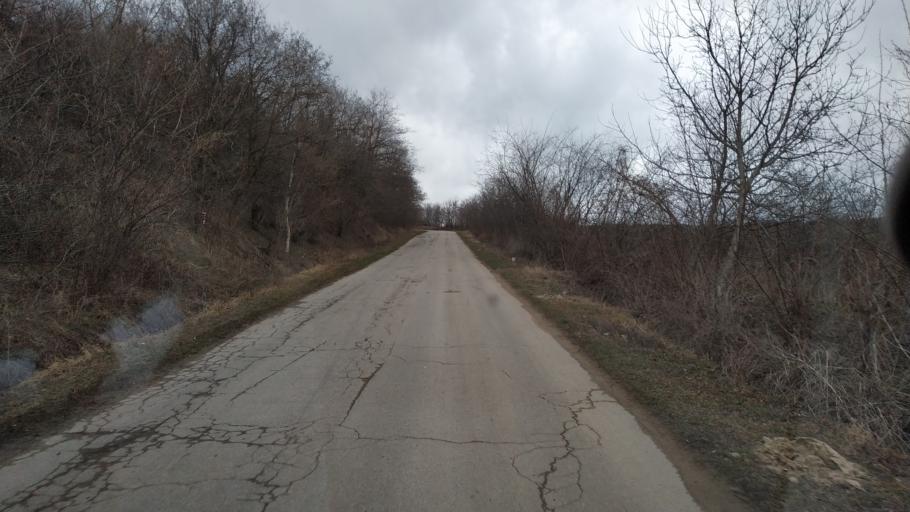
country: MD
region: Calarasi
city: Calarasi
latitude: 47.2157
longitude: 28.2629
